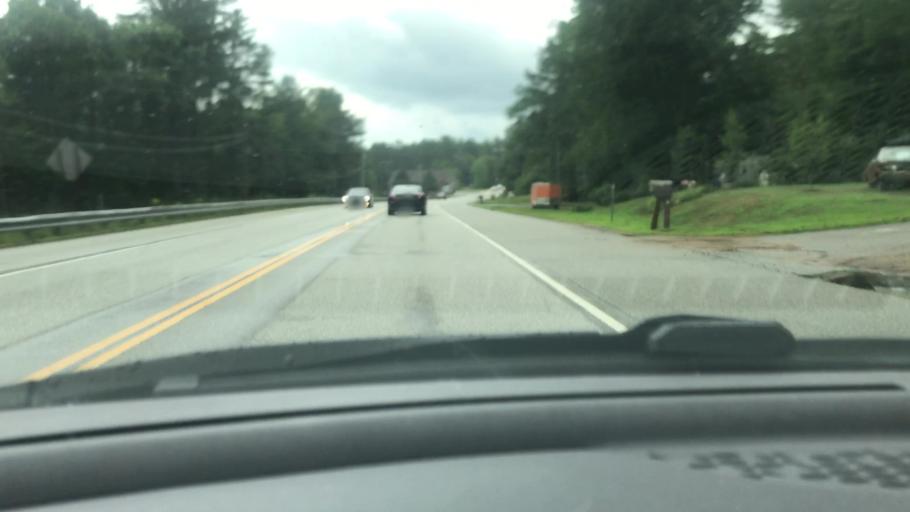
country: US
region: New Hampshire
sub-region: Merrimack County
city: Chichester
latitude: 43.2658
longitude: -71.4583
